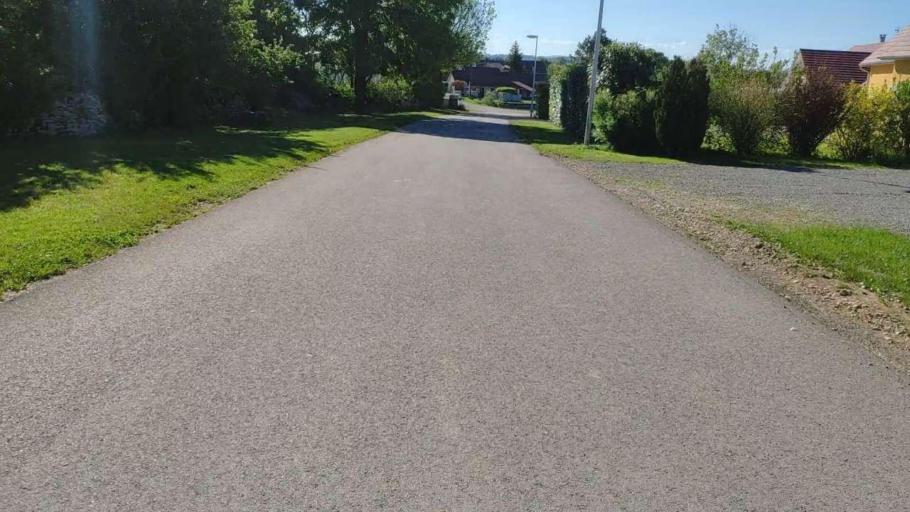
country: FR
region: Franche-Comte
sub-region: Departement du Jura
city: Perrigny
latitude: 46.6865
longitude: 5.6542
